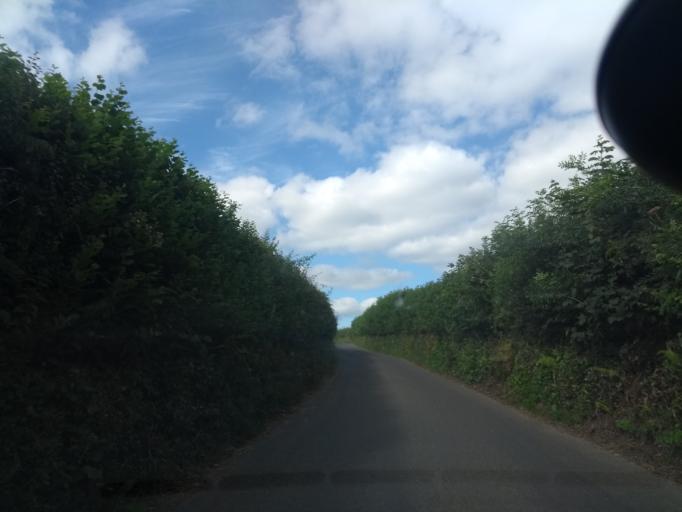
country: GB
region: England
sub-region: Devon
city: Modbury
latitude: 50.2997
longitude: -3.8895
